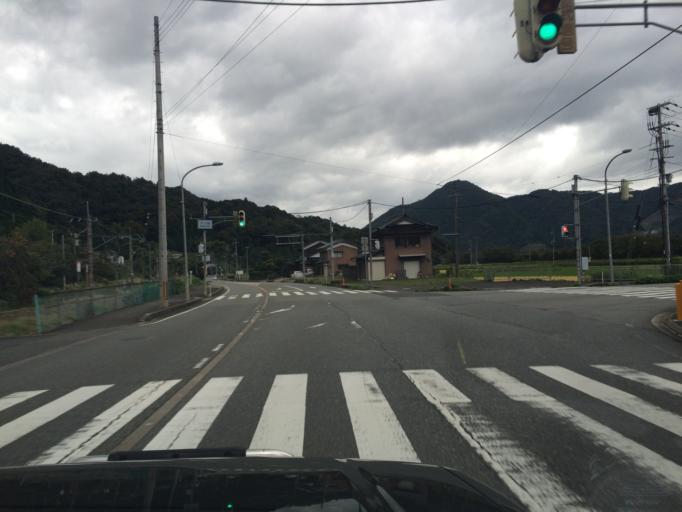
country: JP
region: Hyogo
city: Toyooka
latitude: 35.4244
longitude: 134.7899
